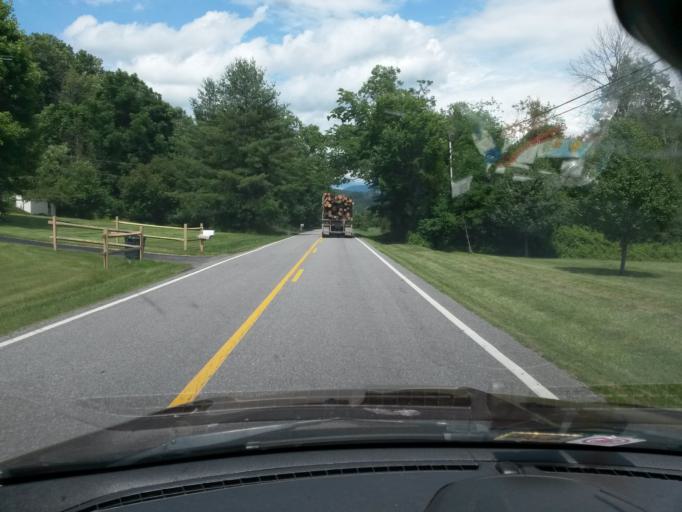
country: US
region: Virginia
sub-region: City of Covington
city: Covington
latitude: 37.7944
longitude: -80.0849
